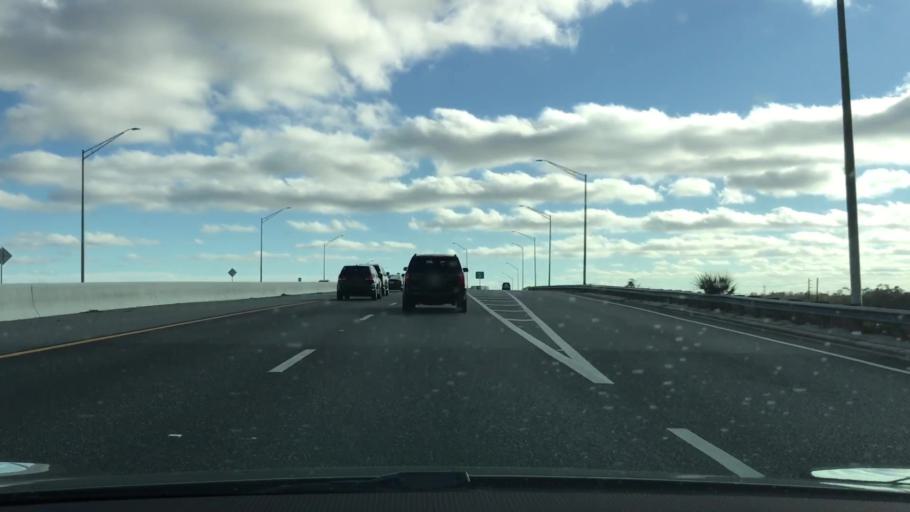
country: US
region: Florida
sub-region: Orange County
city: Meadow Woods
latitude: 28.3851
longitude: -81.3087
